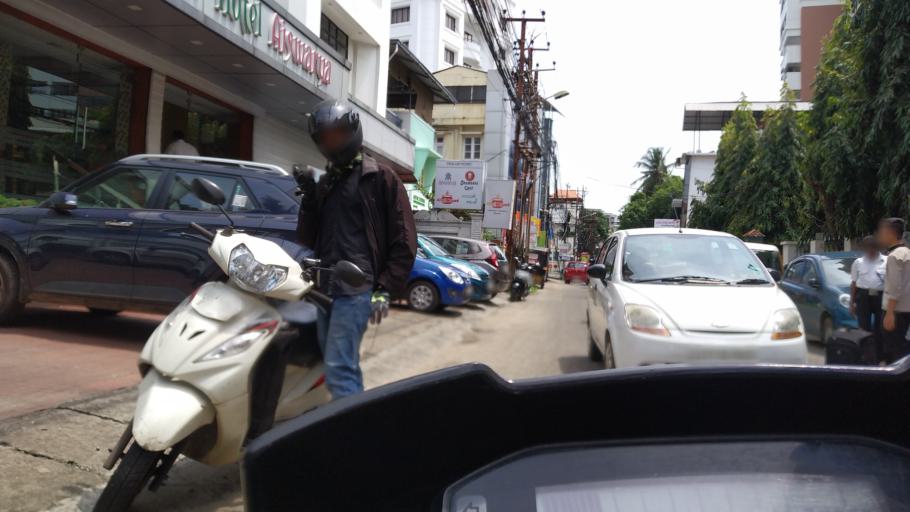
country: IN
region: Kerala
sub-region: Ernakulam
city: Cochin
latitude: 9.9679
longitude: 76.2848
